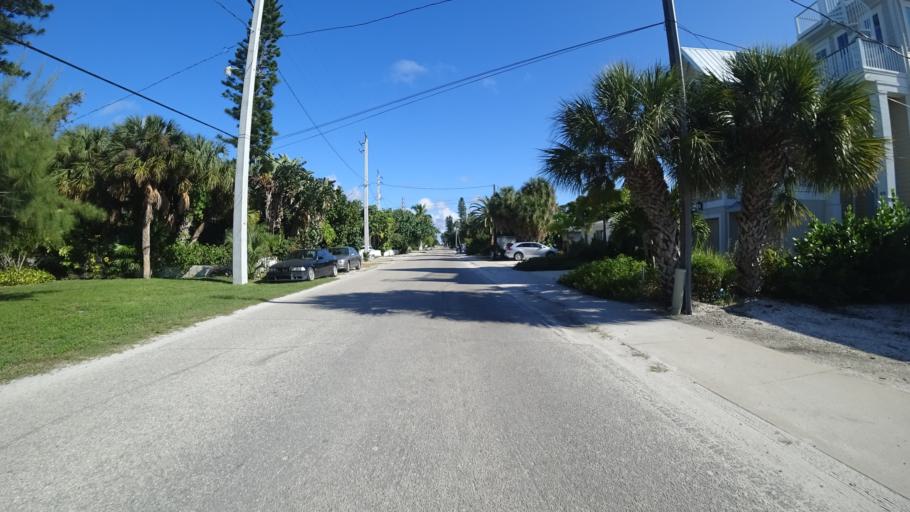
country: US
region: Florida
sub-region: Manatee County
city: Anna Maria
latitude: 27.5368
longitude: -82.7402
